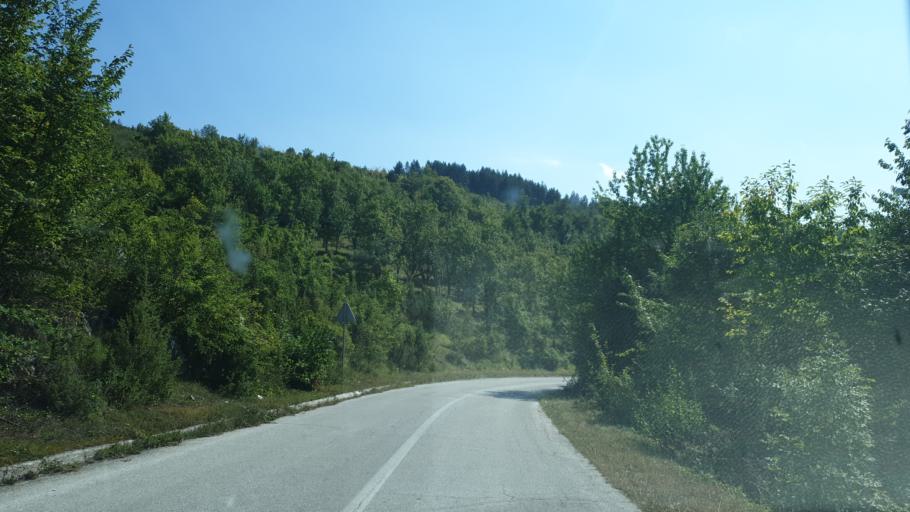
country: RS
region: Central Serbia
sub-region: Zlatiborski Okrug
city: Cajetina
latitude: 43.6824
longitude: 19.8509
